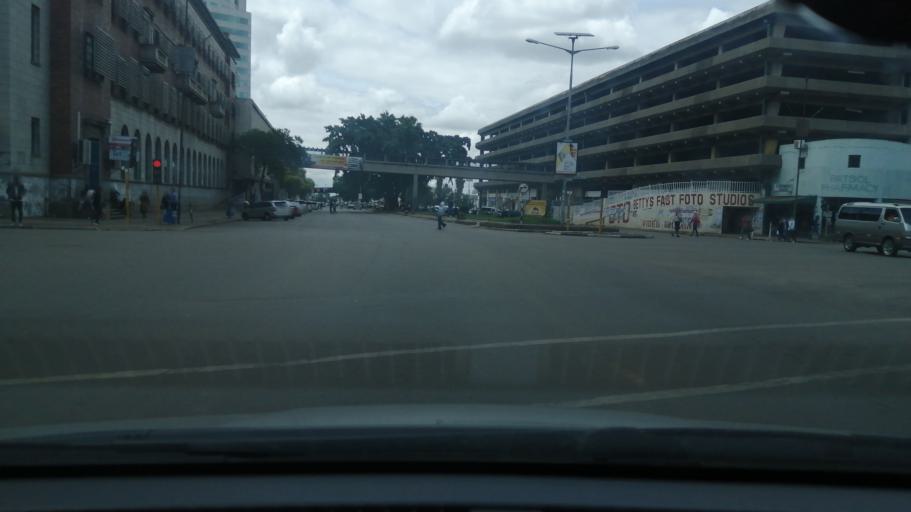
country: ZW
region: Harare
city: Harare
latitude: -17.8294
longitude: 31.0470
